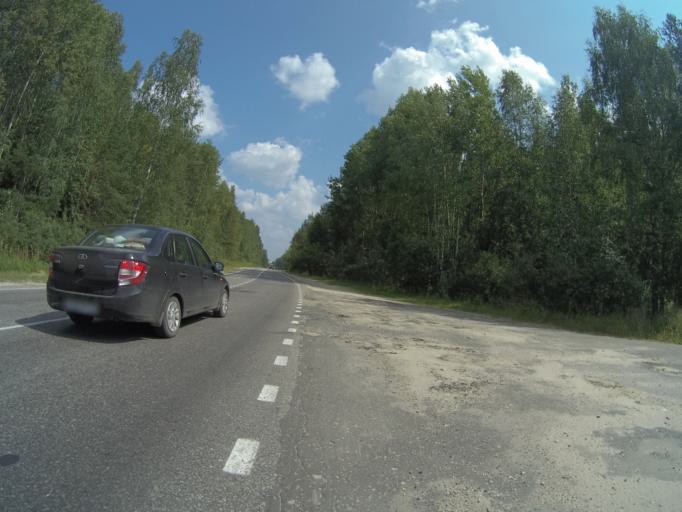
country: RU
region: Vladimir
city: Gus'-Khrustal'nyy
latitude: 55.6355
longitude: 40.7166
